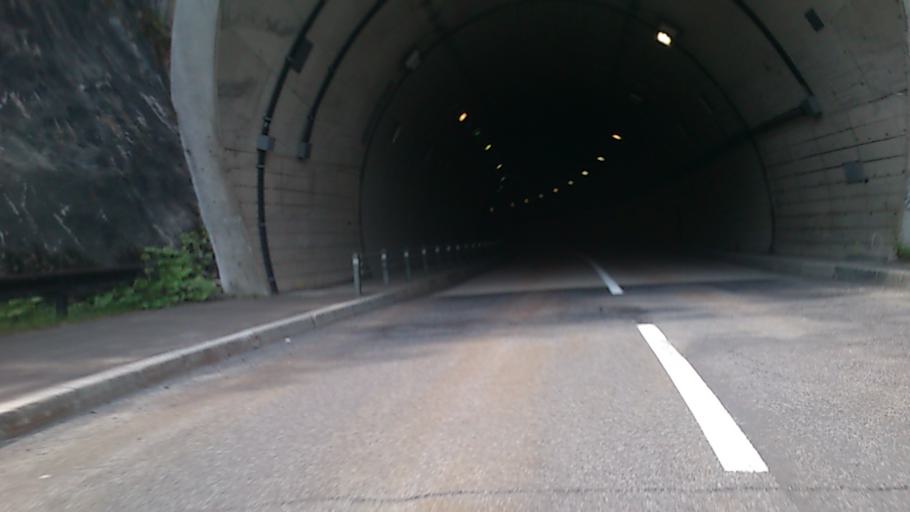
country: JP
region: Hokkaido
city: Kamikawa
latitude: 43.6747
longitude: 143.0354
